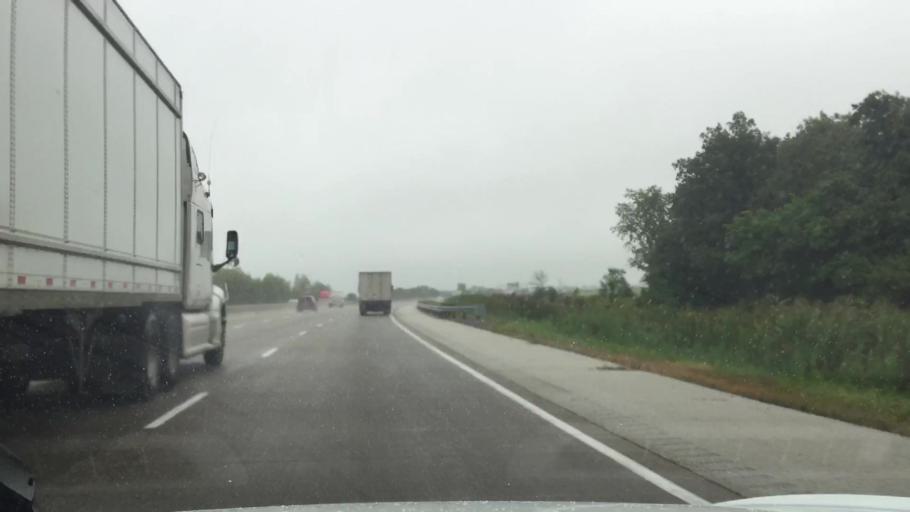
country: US
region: Michigan
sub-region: Wayne County
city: Grosse Pointe Farms
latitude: 42.2420
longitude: -82.5768
